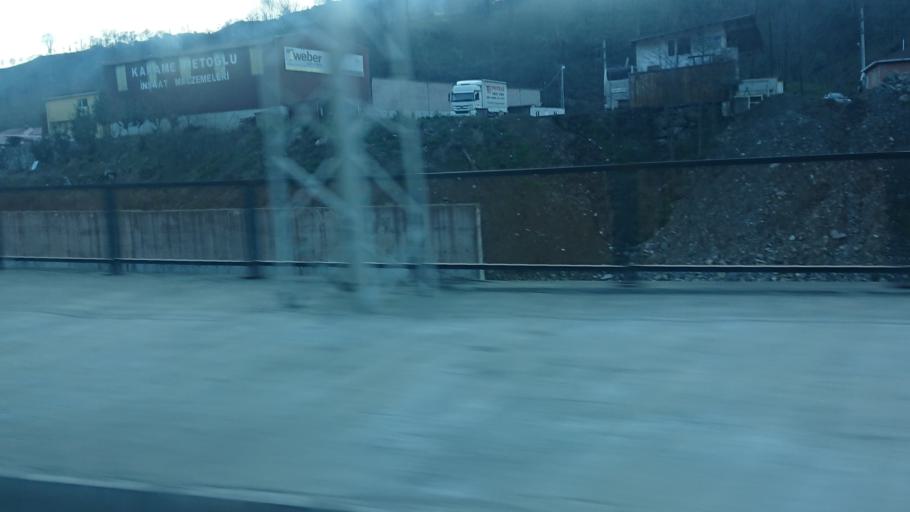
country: TR
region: Rize
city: Gundogdu
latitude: 41.0299
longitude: 40.5835
